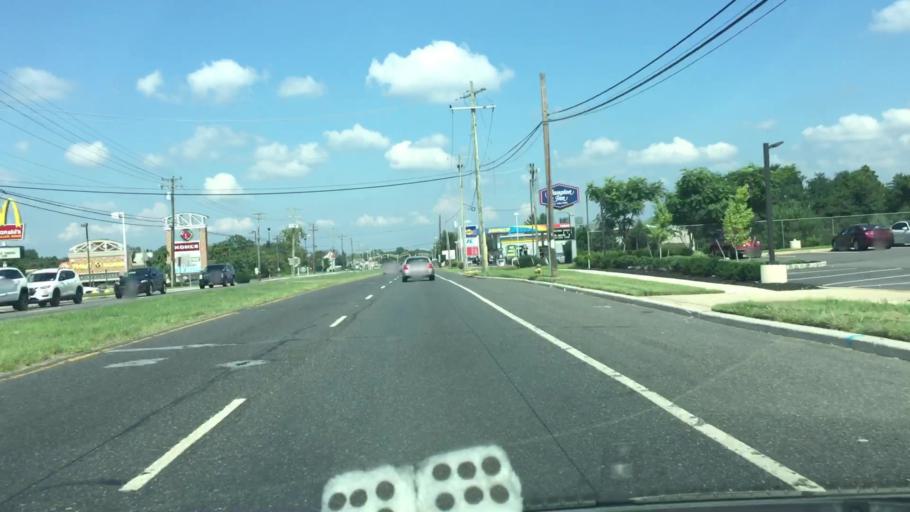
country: US
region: New Jersey
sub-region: Gloucester County
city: Turnersville
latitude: 39.7613
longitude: -75.0477
